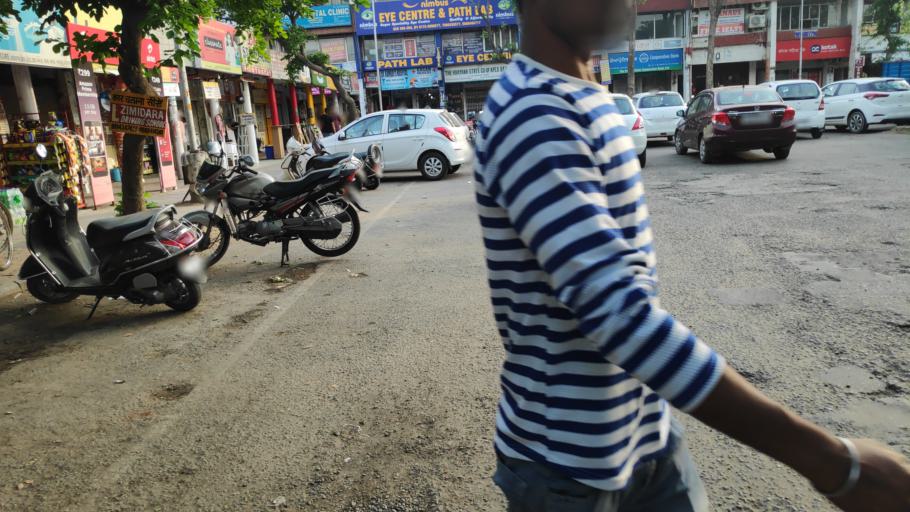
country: IN
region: Chandigarh
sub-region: Chandigarh
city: Chandigarh
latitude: 30.7145
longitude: 76.7518
